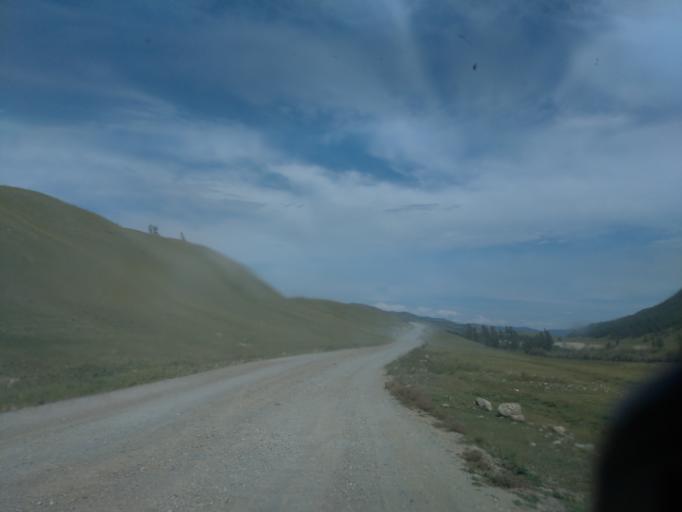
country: RU
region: Altay
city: Ust'-Ulagan
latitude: 50.7065
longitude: 88.0161
